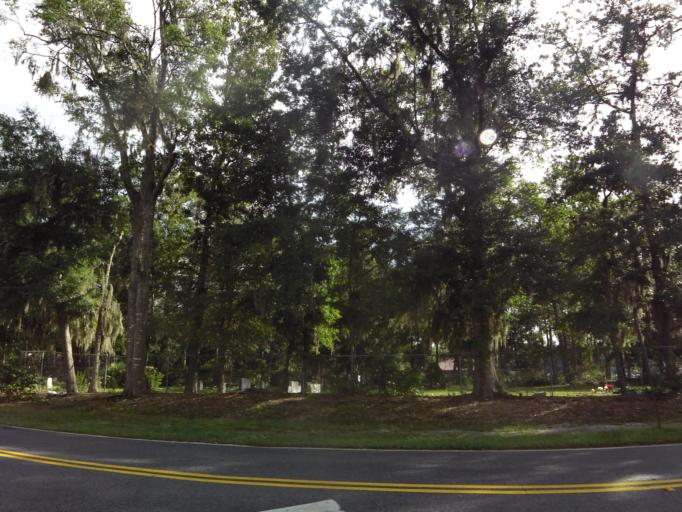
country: US
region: Georgia
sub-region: Liberty County
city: Walthourville
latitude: 31.7958
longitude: -81.6063
